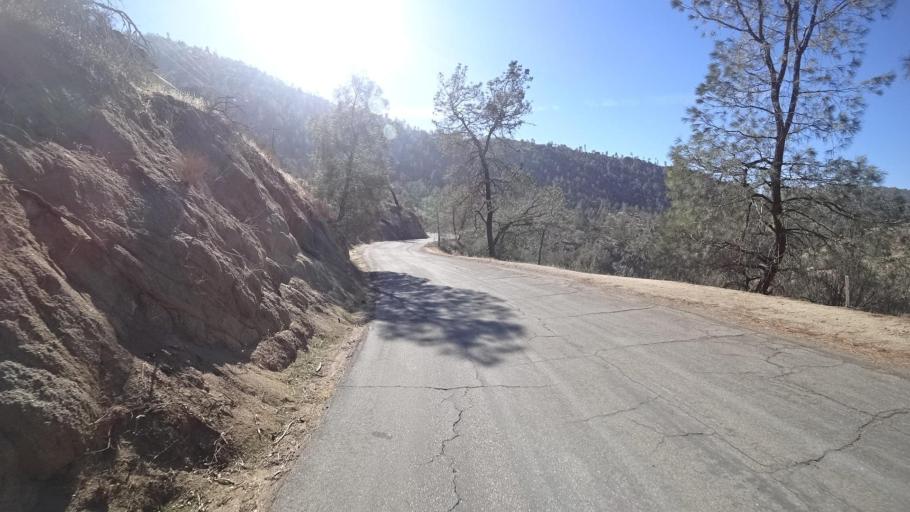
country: US
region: California
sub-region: Kern County
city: Bodfish
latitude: 35.5686
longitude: -118.5670
